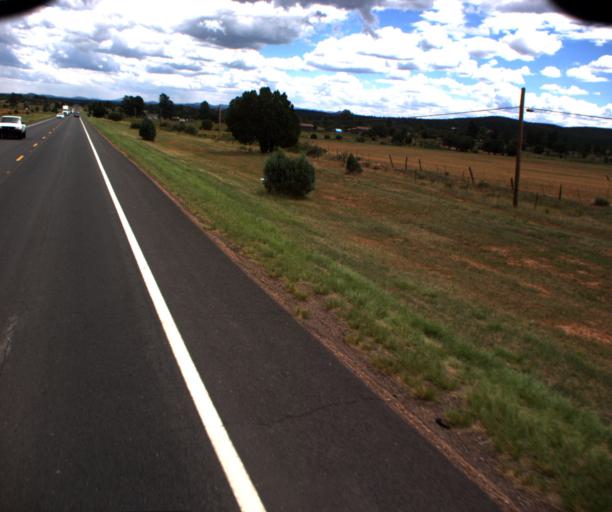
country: US
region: Arizona
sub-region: Navajo County
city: Linden
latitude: 34.2853
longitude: -110.1630
